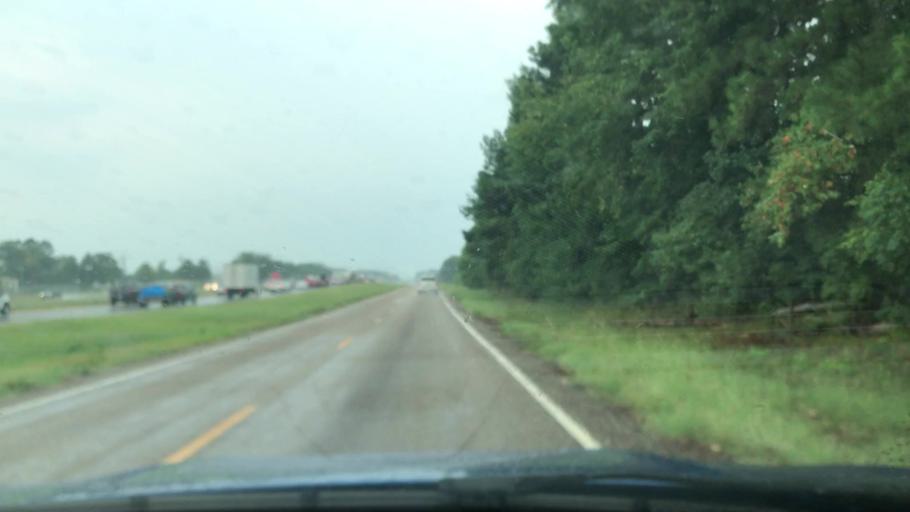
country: US
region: Texas
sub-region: Harrison County
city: Waskom
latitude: 32.4889
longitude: -94.1408
